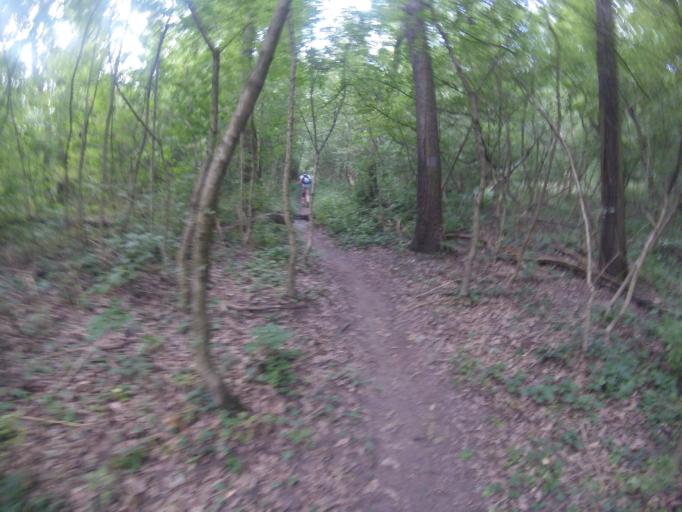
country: HU
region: Veszprem
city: Badacsonytomaj
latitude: 46.8298
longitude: 17.5047
